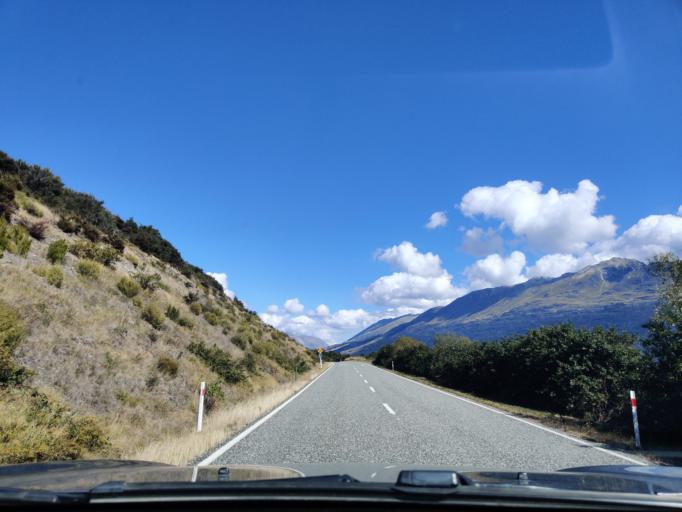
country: NZ
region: Otago
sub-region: Queenstown-Lakes District
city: Queenstown
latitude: -44.9883
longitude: 168.4322
